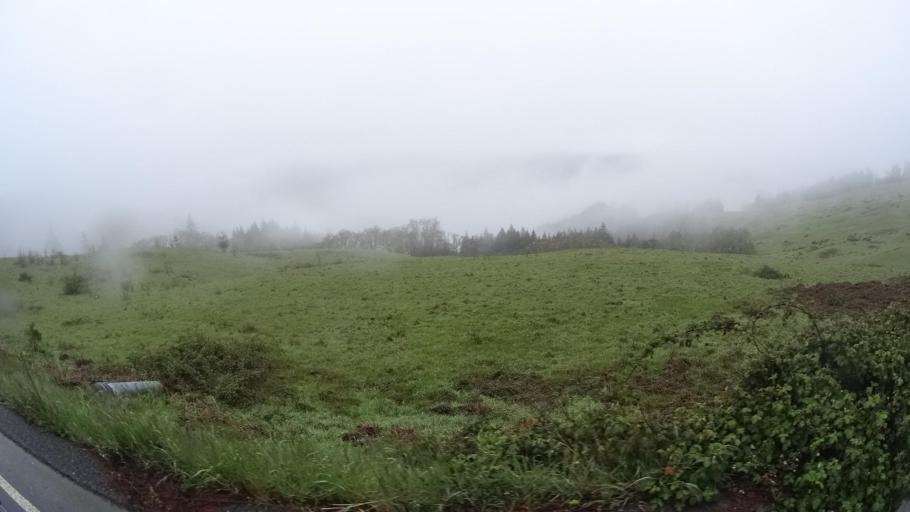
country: US
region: California
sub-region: Humboldt County
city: Westhaven-Moonstone
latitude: 41.1875
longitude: -123.9291
